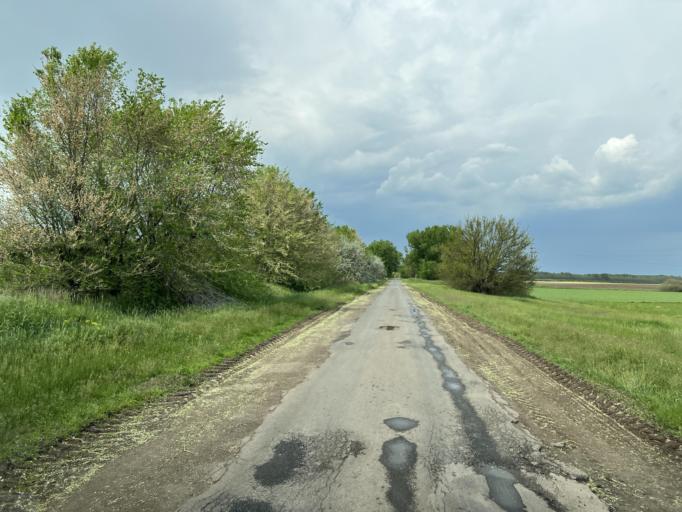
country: HU
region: Pest
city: Nagykoros
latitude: 46.9843
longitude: 19.8057
